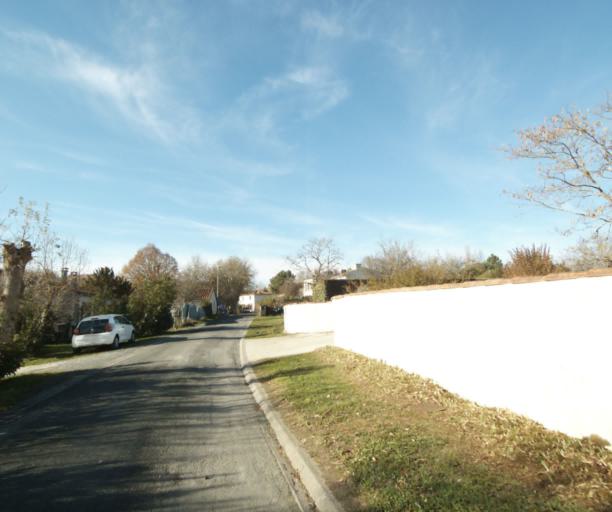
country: FR
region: Poitou-Charentes
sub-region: Departement de la Charente-Maritime
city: Ecoyeux
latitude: 45.7701
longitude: -0.5029
